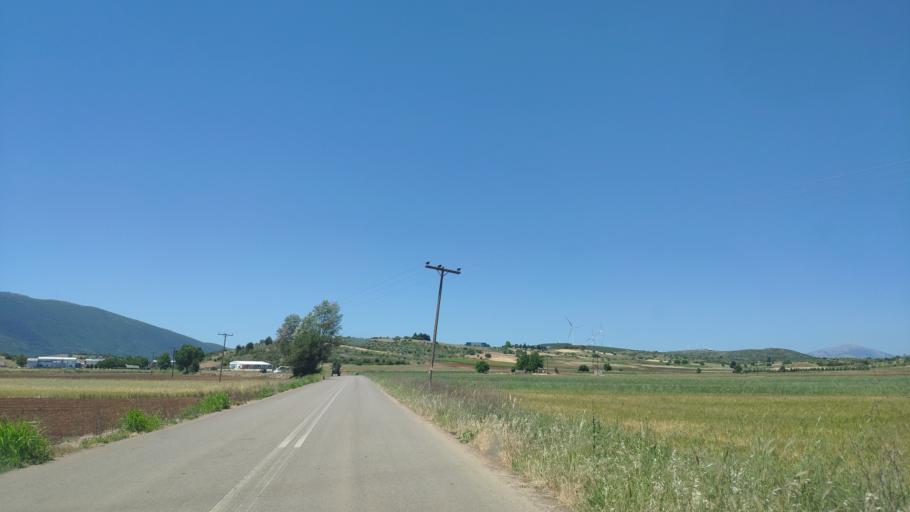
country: GR
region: Central Greece
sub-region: Nomos Voiotias
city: Kaparellion
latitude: 38.2448
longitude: 23.2370
